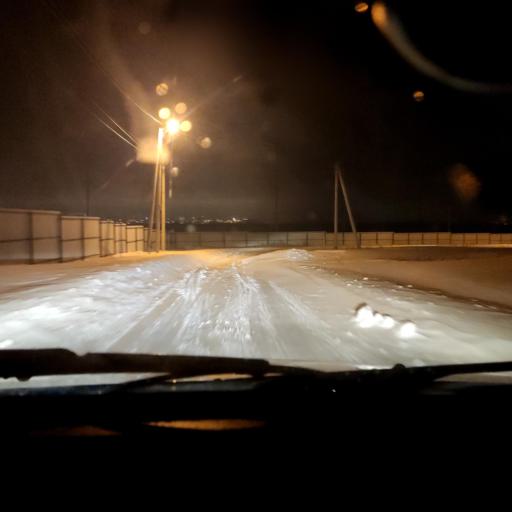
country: RU
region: Bashkortostan
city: Mikhaylovka
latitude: 54.7853
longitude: 55.8028
